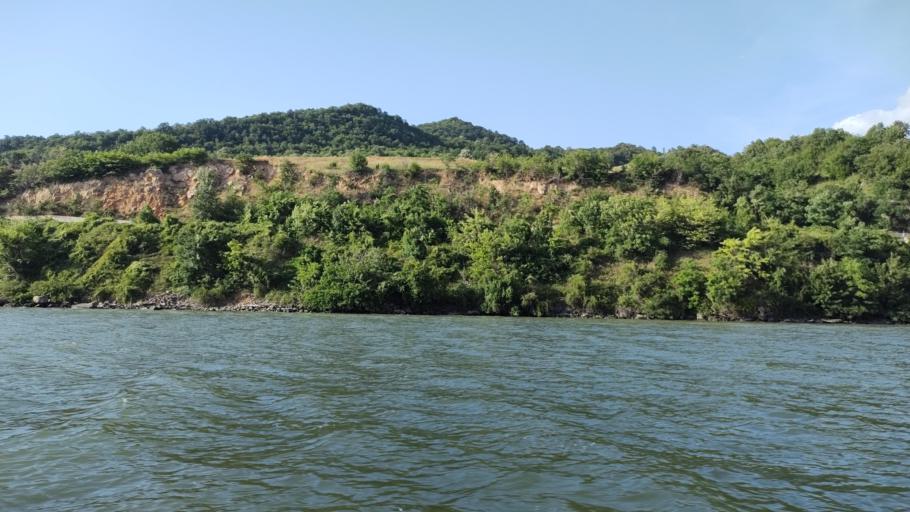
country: RO
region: Mehedinti
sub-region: Comuna Svinita
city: Svinita
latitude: 44.4806
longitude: 22.1260
